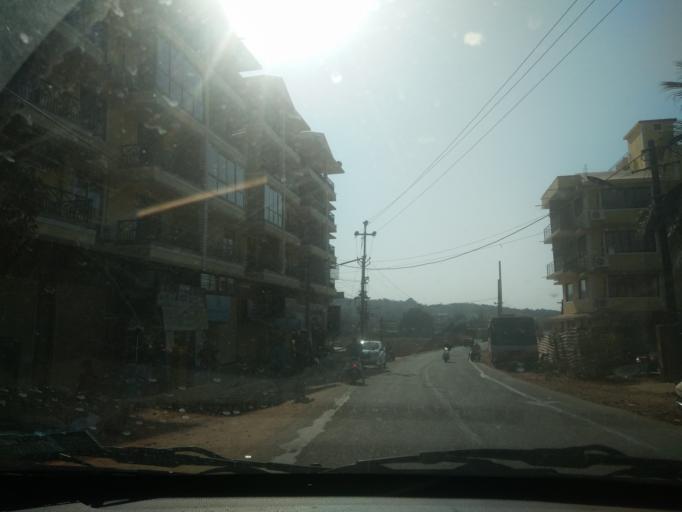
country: IN
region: Goa
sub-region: South Goa
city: Chicalim
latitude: 15.3878
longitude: 73.8499
